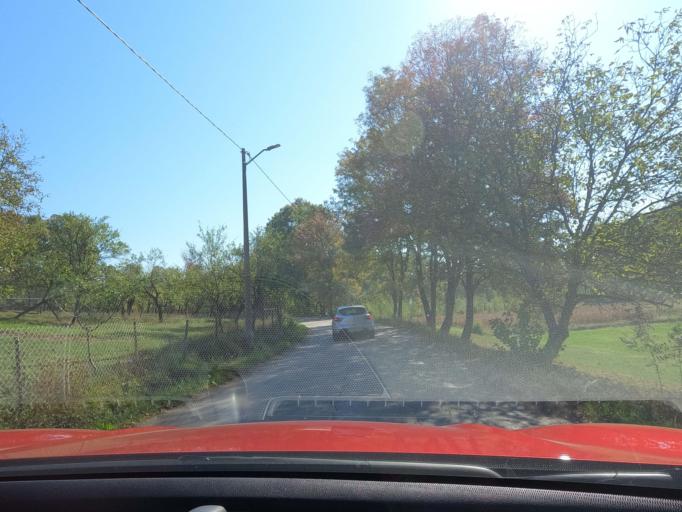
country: RS
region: Central Serbia
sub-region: Raski Okrug
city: Kraljevo
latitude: 43.7720
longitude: 20.6565
